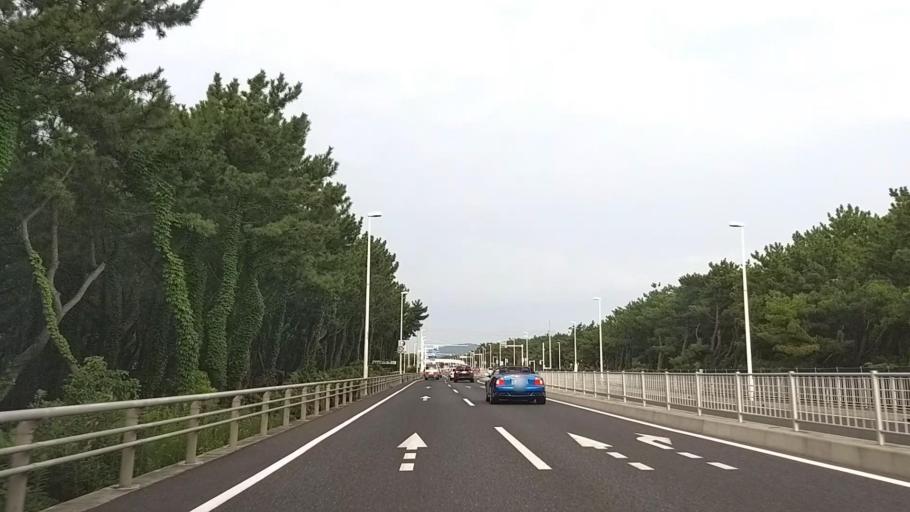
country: JP
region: Kanagawa
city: Hiratsuka
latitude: 35.3159
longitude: 139.3510
